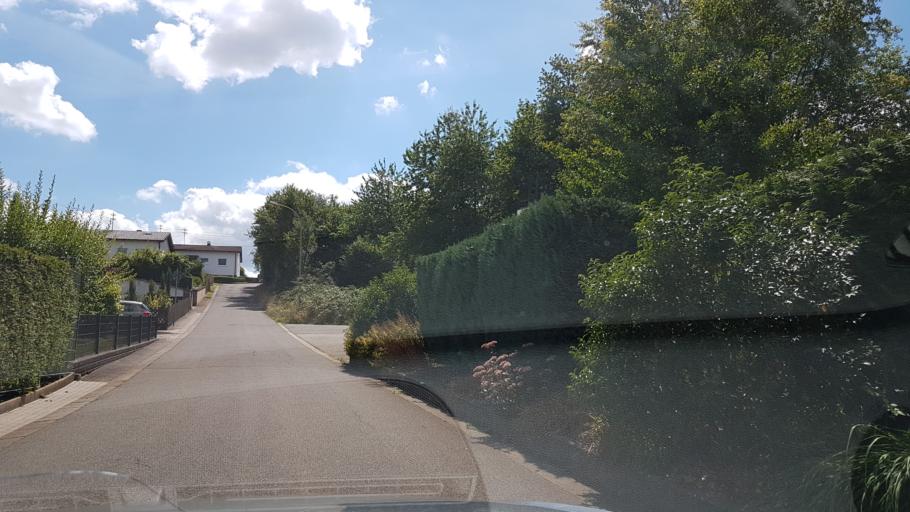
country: DE
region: Saarland
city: Illingen
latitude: 49.3750
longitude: 7.0402
